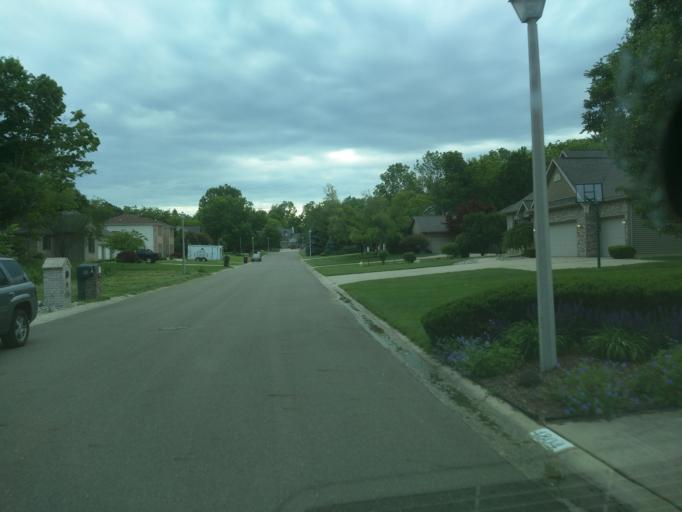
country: US
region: Michigan
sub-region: Eaton County
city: Waverly
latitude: 42.7523
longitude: -84.6170
